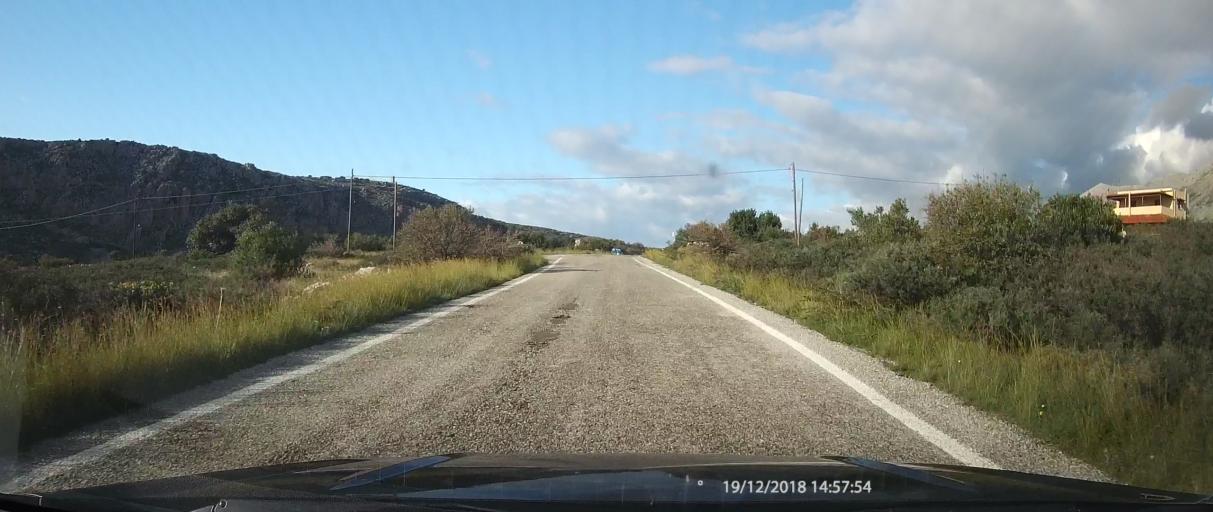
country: GR
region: Peloponnese
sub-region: Nomos Lakonias
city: Gytheio
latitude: 36.4835
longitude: 22.4039
